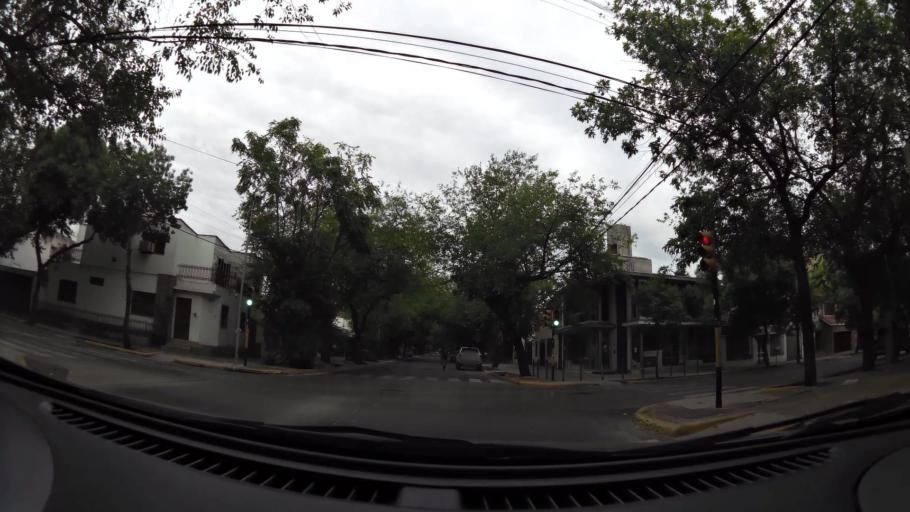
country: AR
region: Mendoza
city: Mendoza
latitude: -32.9020
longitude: -68.8514
